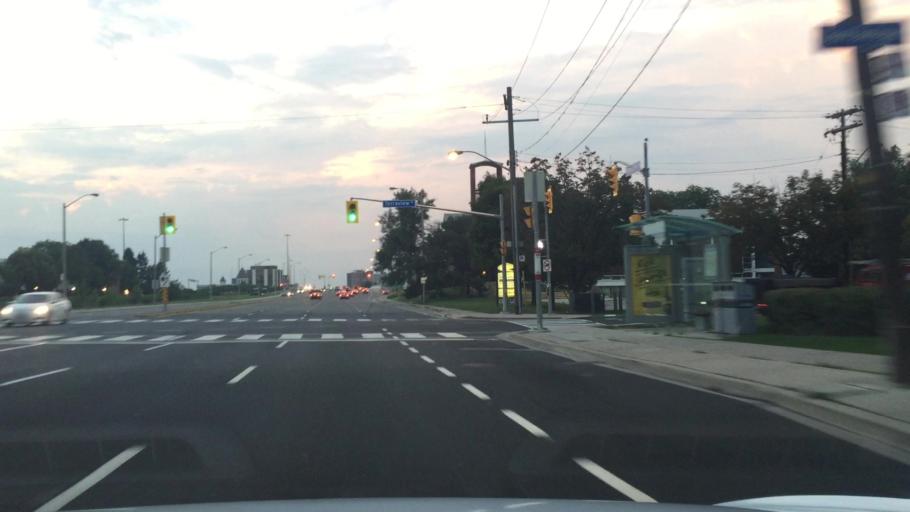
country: CA
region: Ontario
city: Scarborough
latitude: 43.7643
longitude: -79.3179
